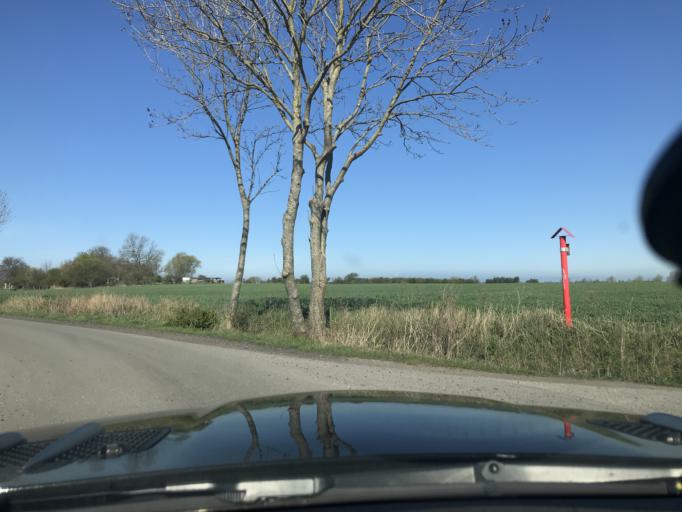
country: DE
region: Schleswig-Holstein
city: Grossenbrode
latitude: 54.4394
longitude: 11.1116
